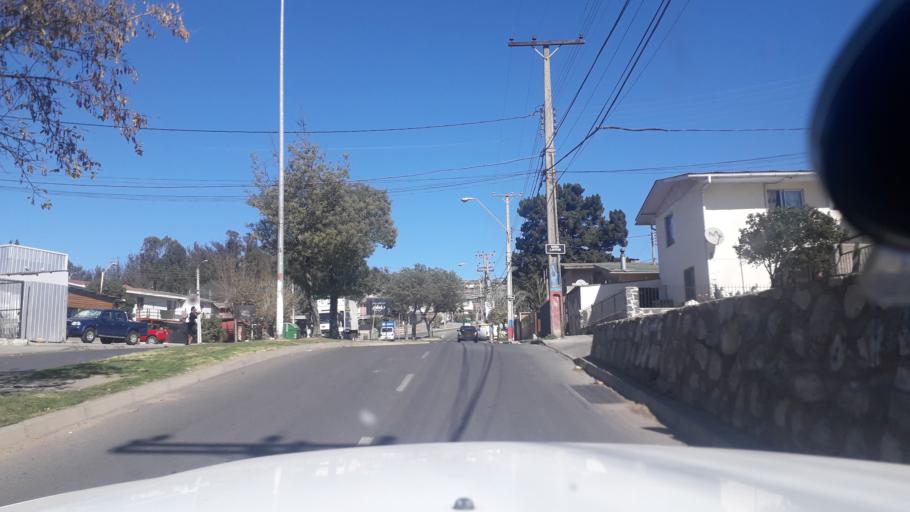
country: CL
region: Valparaiso
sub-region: Provincia de Valparaiso
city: Vina del Mar
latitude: -33.0382
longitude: -71.5077
